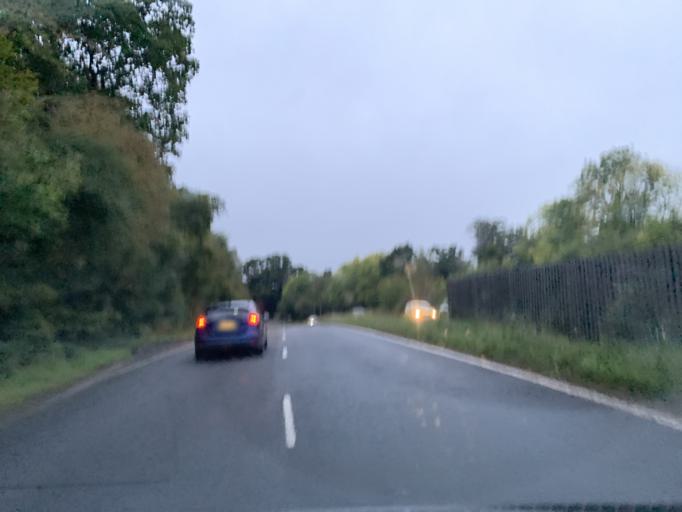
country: GB
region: England
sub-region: Hampshire
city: Cadnam
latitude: 50.9207
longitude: -1.5827
